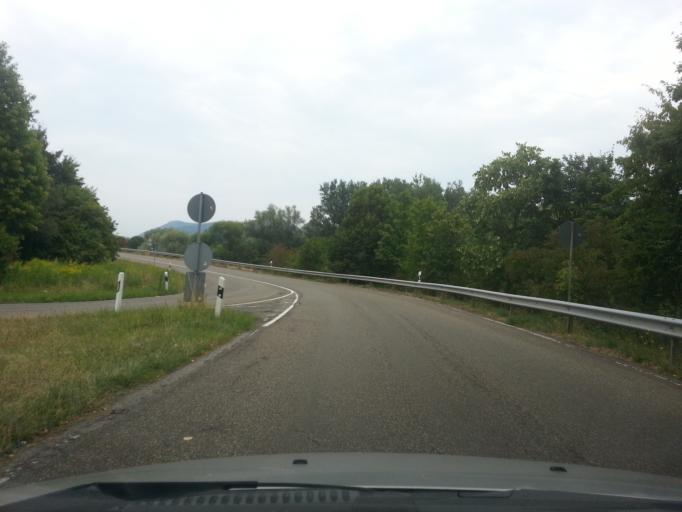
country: DE
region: Rheinland-Pfalz
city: Siebeldingen
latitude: 49.2056
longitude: 8.0830
